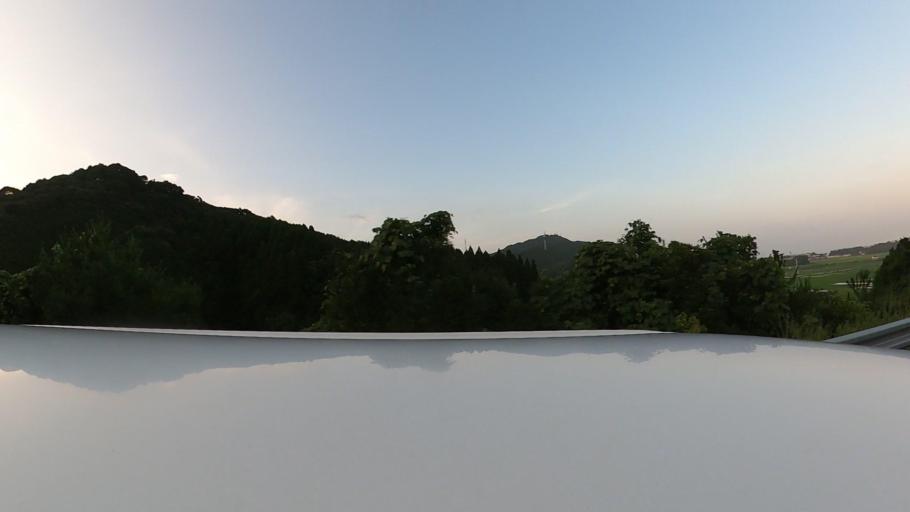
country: JP
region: Miyazaki
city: Nobeoka
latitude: 32.5452
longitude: 131.6474
